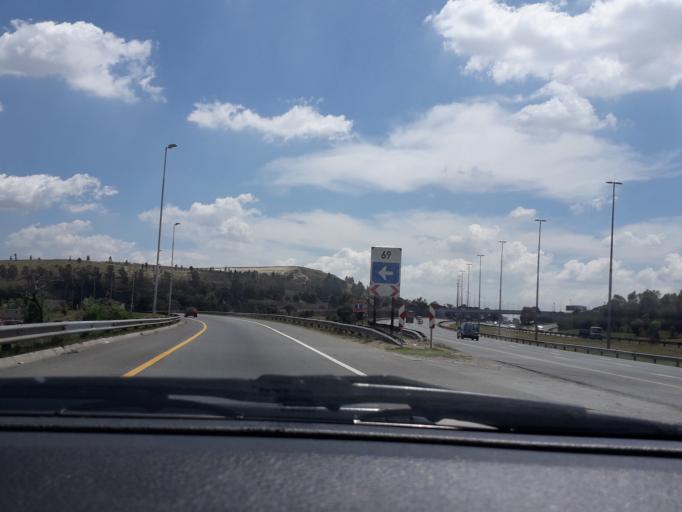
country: ZA
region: Gauteng
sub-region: City of Johannesburg Metropolitan Municipality
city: Johannesburg
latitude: -26.2376
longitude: 27.9606
